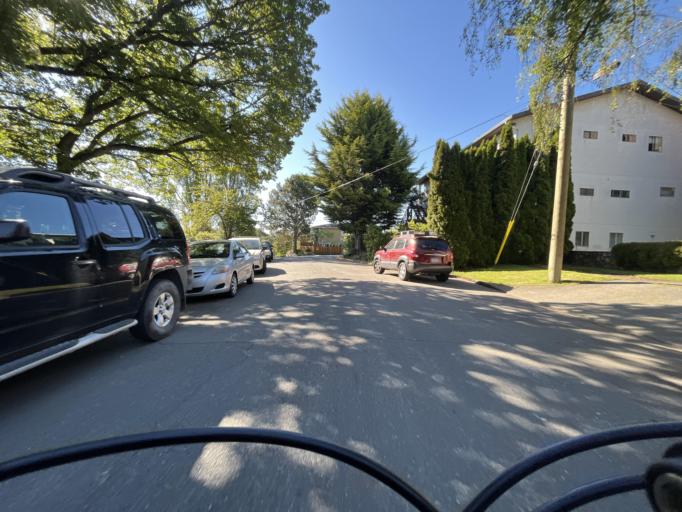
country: CA
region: British Columbia
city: Victoria
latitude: 48.4397
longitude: -123.3898
